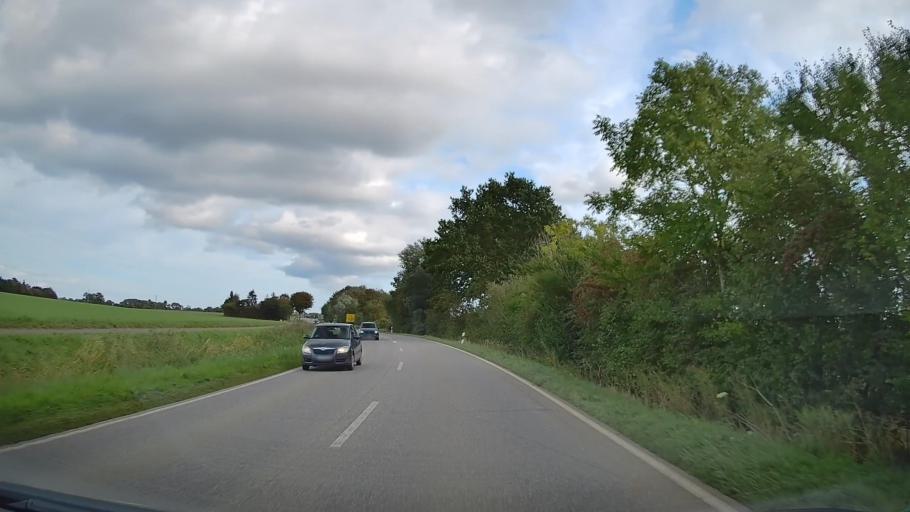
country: DE
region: Schleswig-Holstein
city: Niesgrau
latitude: 54.7511
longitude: 9.8151
